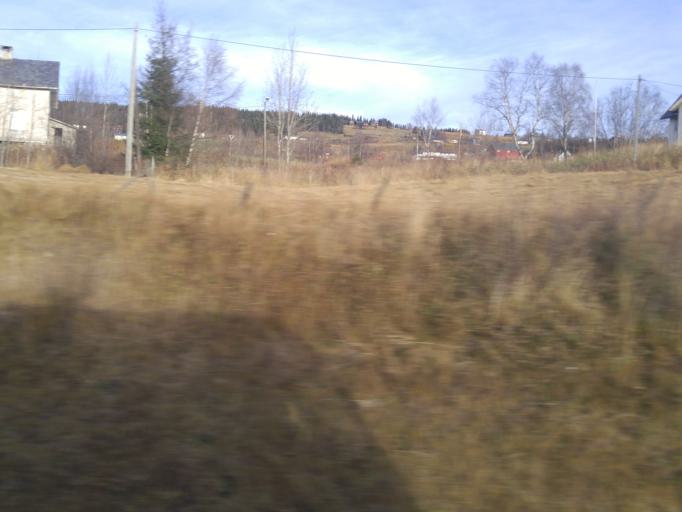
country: NO
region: Oppland
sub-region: Nord-Aurdal
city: Fagernes
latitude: 61.0635
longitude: 9.1611
